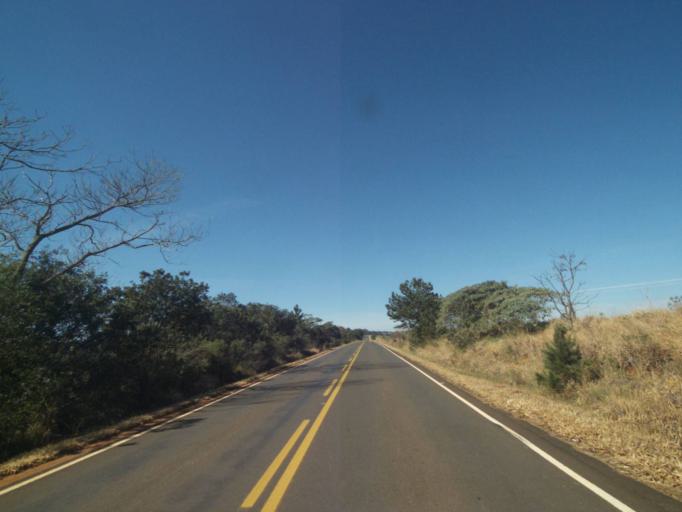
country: BR
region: Parana
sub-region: Tibagi
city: Tibagi
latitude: -24.4874
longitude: -50.4708
